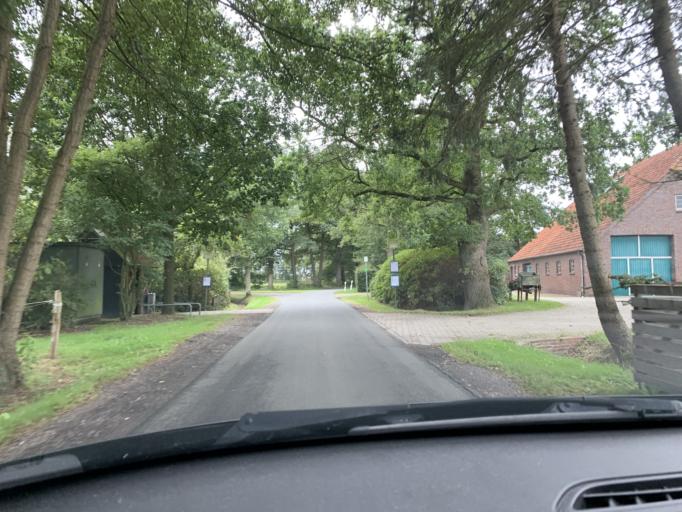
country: DE
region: Lower Saxony
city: Westerstede
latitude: 53.2783
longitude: 7.8874
